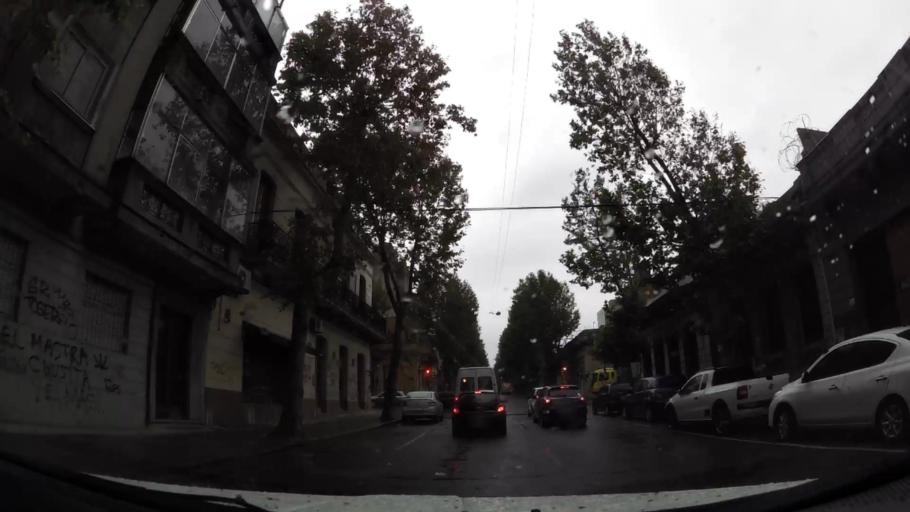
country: UY
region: Montevideo
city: Montevideo
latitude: -34.9084
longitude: -56.1735
